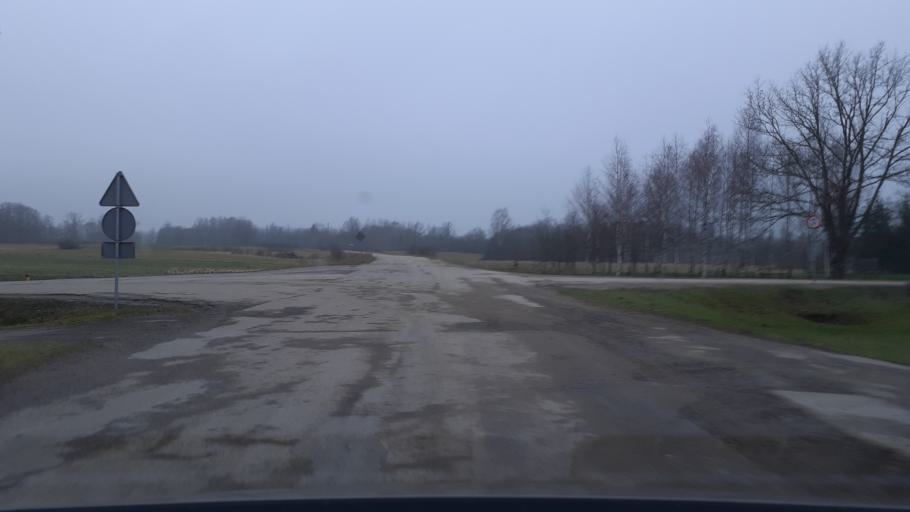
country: LV
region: Talsu Rajons
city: Sabile
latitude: 56.9555
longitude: 22.3940
